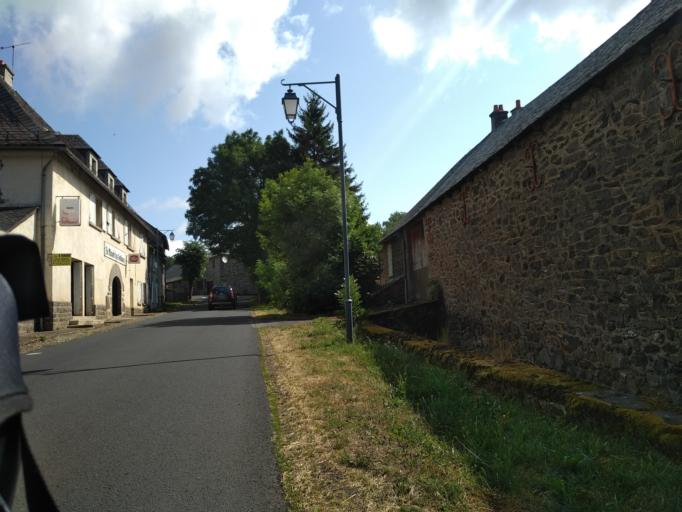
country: FR
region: Auvergne
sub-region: Departement du Cantal
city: Murat
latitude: 45.1572
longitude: 2.7859
